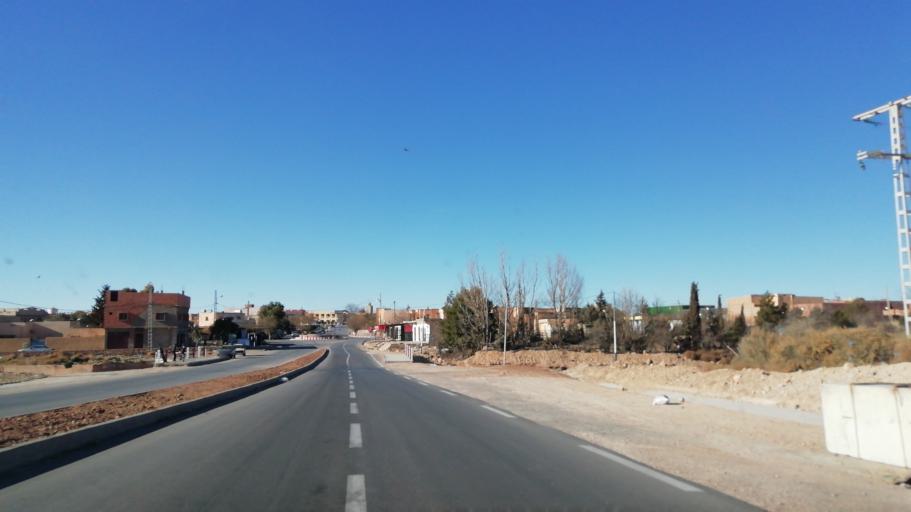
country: DZ
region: Tlemcen
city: Sebdou
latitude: 34.2232
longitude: -1.2522
